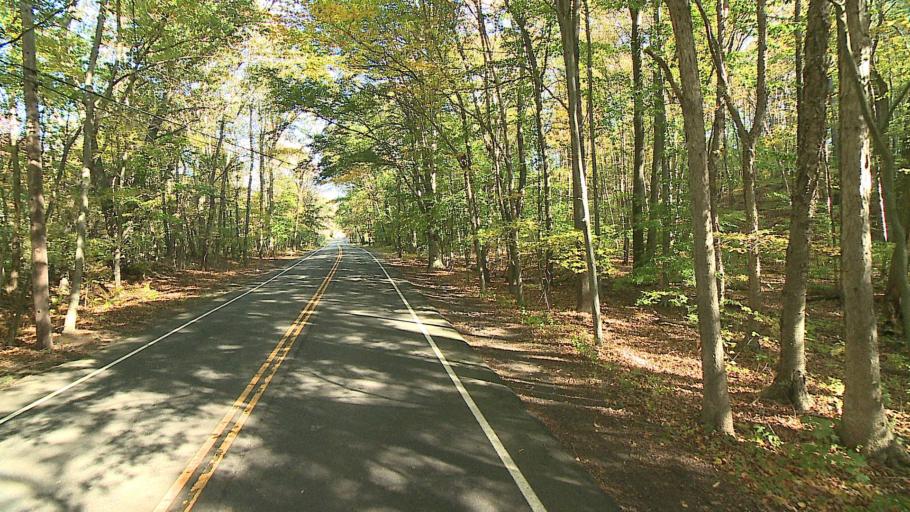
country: US
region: Connecticut
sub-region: Fairfield County
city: Trumbull
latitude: 41.2668
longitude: -73.2984
